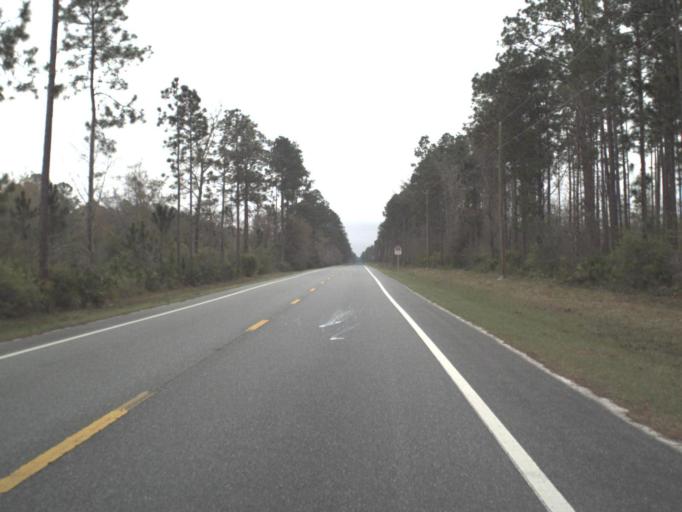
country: US
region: Florida
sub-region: Gulf County
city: Wewahitchka
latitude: 30.0122
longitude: -84.9788
